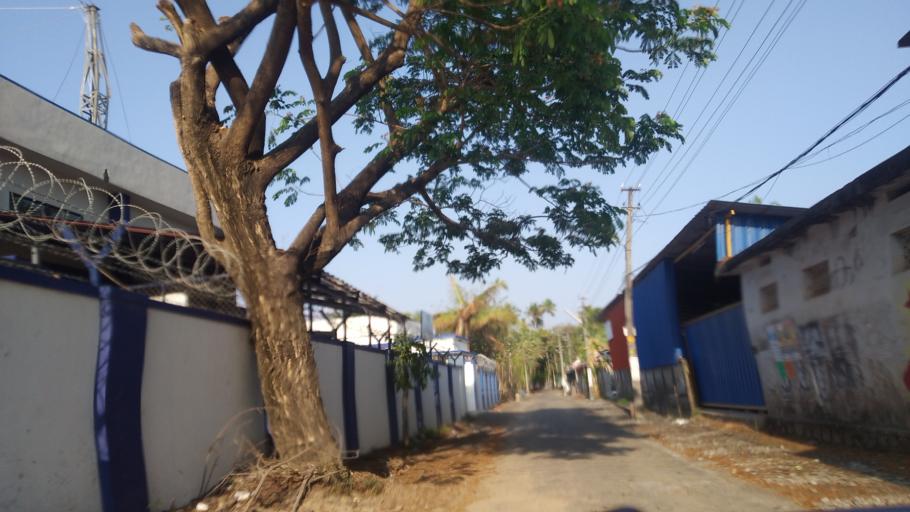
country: IN
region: Kerala
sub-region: Thrissur District
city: Kodungallur
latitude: 10.1268
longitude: 76.2004
